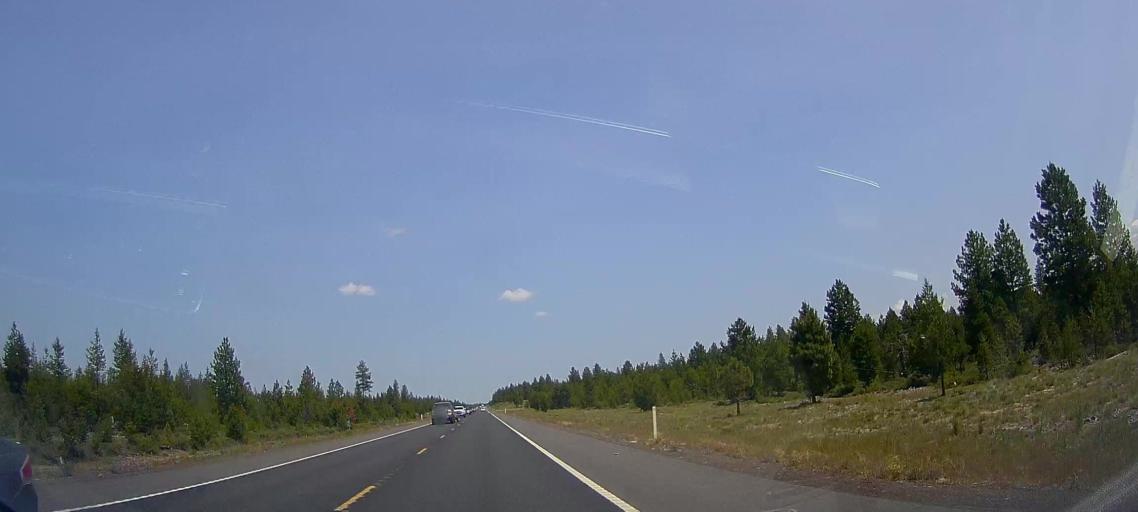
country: US
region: Oregon
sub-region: Deschutes County
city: La Pine
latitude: 43.5044
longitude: -121.6645
